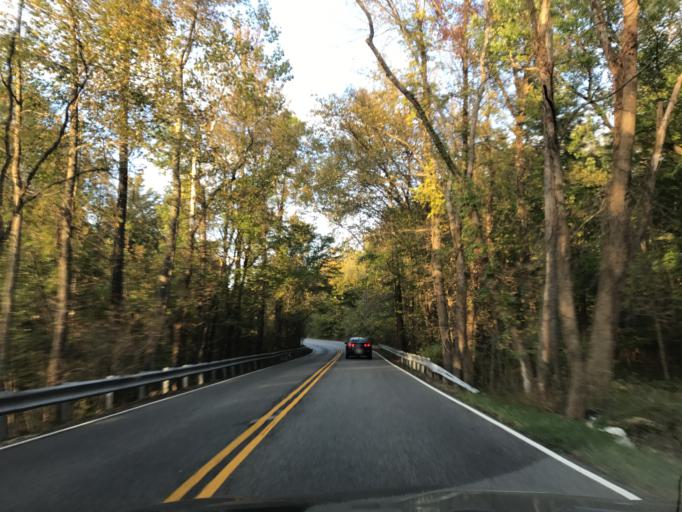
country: US
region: Maryland
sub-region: Anne Arundel County
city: Maryland City
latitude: 39.0771
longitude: -76.8256
